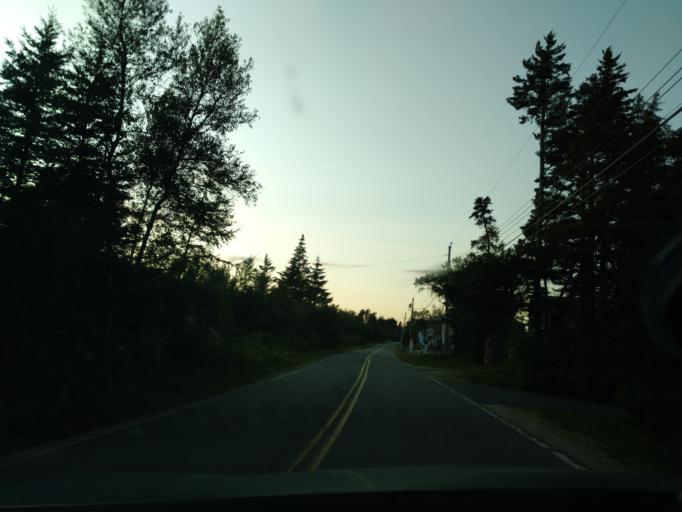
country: US
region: Maine
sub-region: Hancock County
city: Gouldsboro
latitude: 44.3721
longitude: -68.0339
